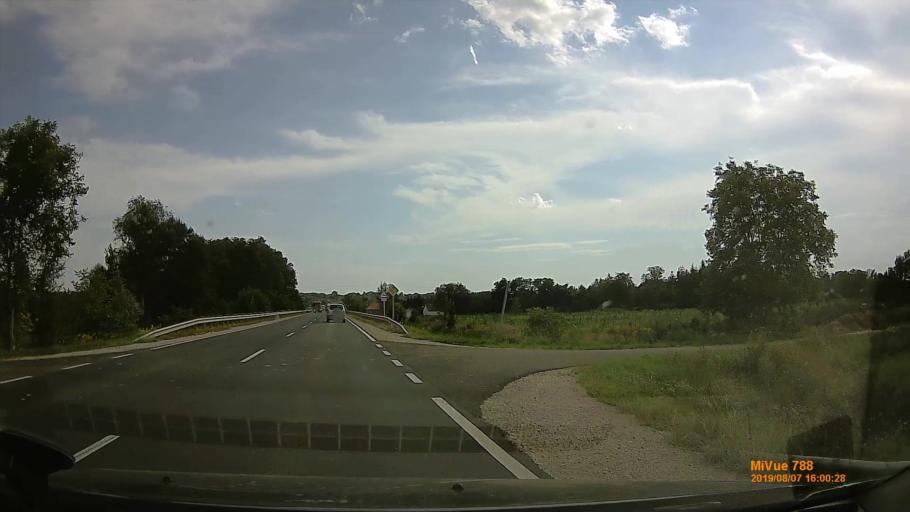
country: HU
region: Vas
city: Kormend
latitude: 47.0019
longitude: 16.6157
